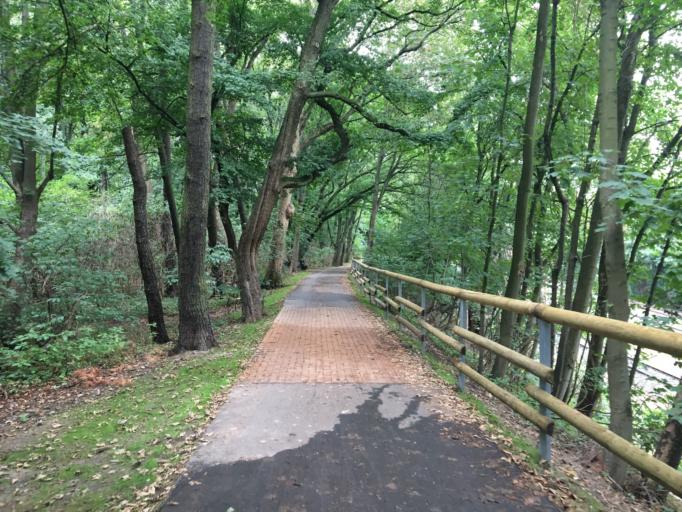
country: DE
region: Lower Saxony
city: Braunschweig
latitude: 52.2726
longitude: 10.5556
